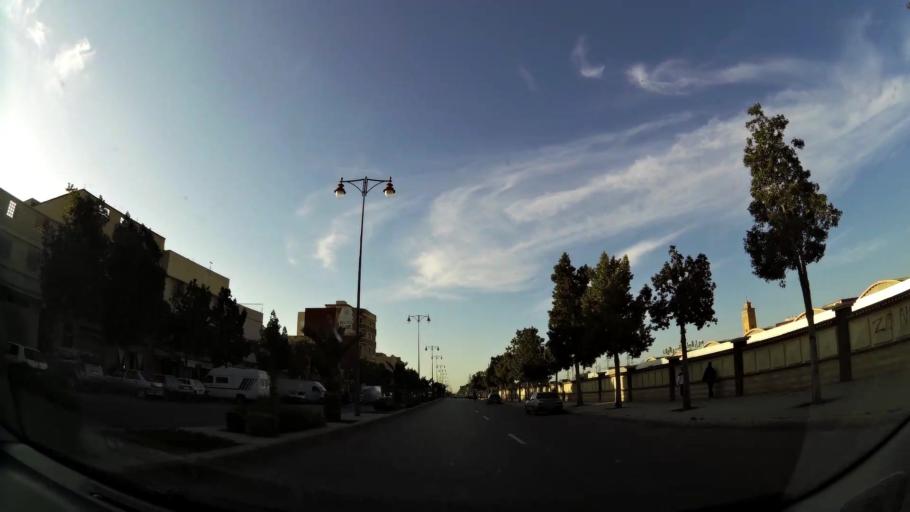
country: MA
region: Oriental
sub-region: Oujda-Angad
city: Oujda
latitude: 34.7010
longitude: -1.9192
